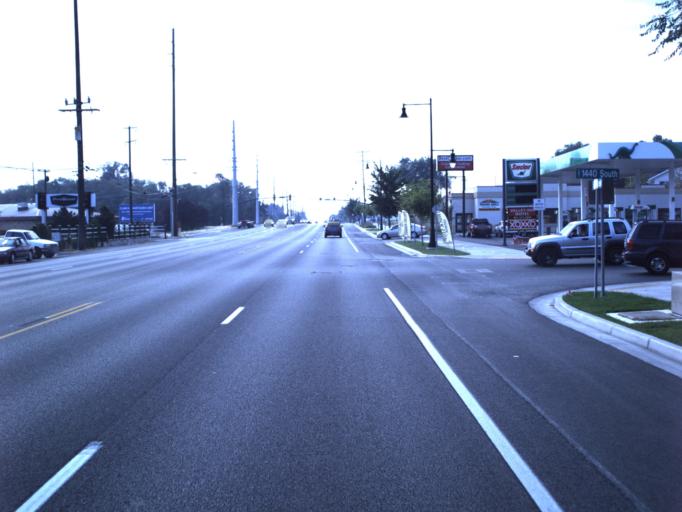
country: US
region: Utah
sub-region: Utah County
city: Provo
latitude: 40.2141
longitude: -111.6347
